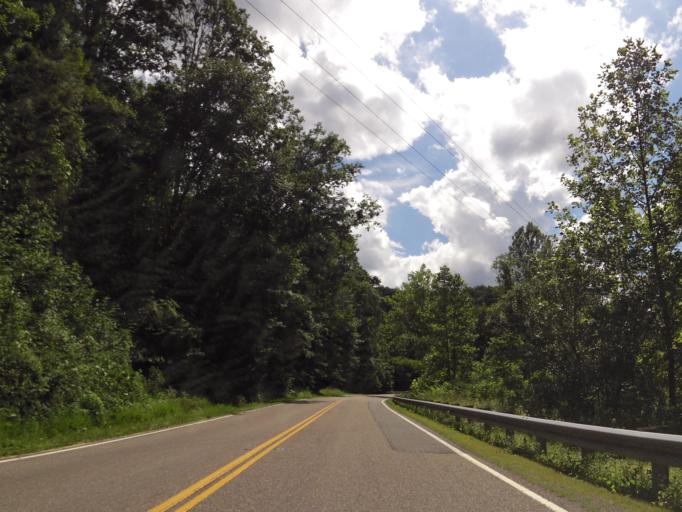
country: US
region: Virginia
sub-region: Lee County
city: Pennington Gap
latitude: 36.7678
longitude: -83.1011
